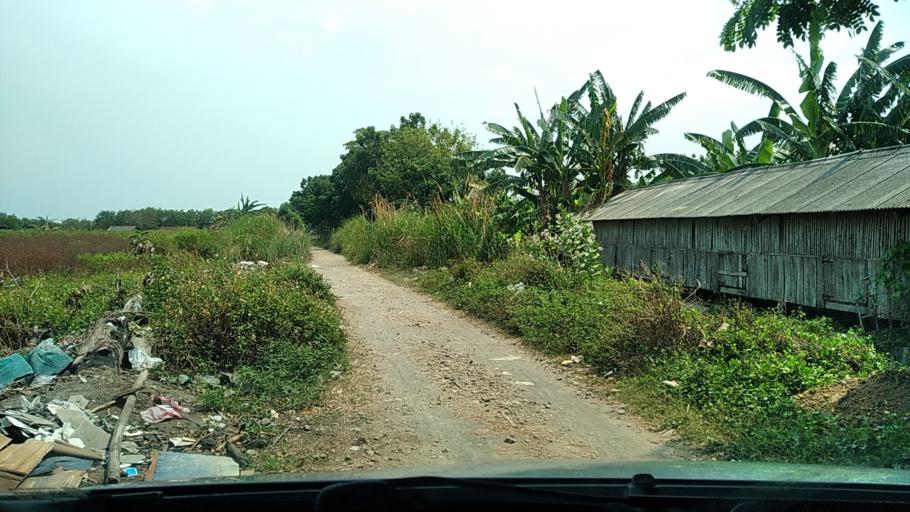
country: ID
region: Central Java
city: Semarang
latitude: -6.9772
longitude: 110.3523
